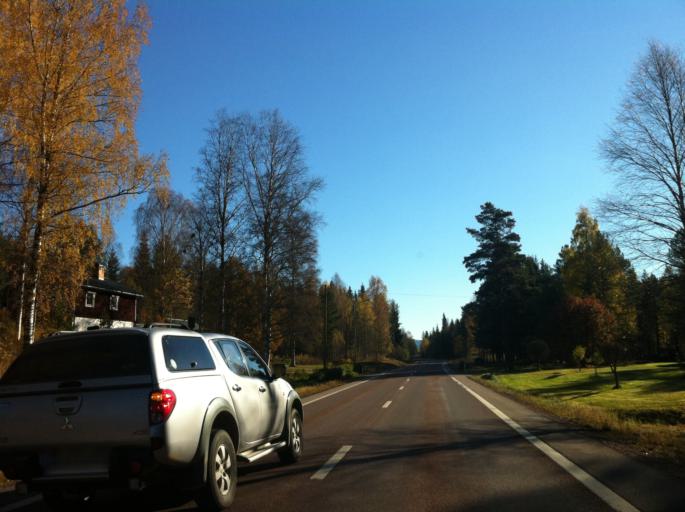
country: SE
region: Dalarna
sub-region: Alvdalens Kommun
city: AElvdalen
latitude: 61.1768
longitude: 14.0997
